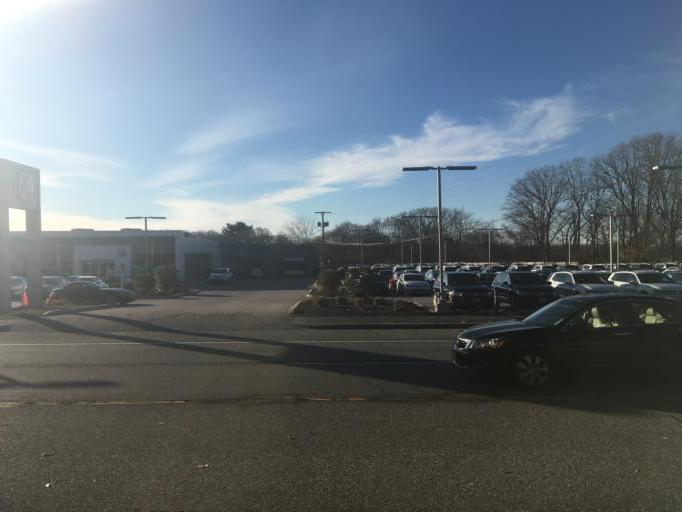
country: US
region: Rhode Island
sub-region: Kent County
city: West Warwick
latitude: 41.6798
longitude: -71.5001
